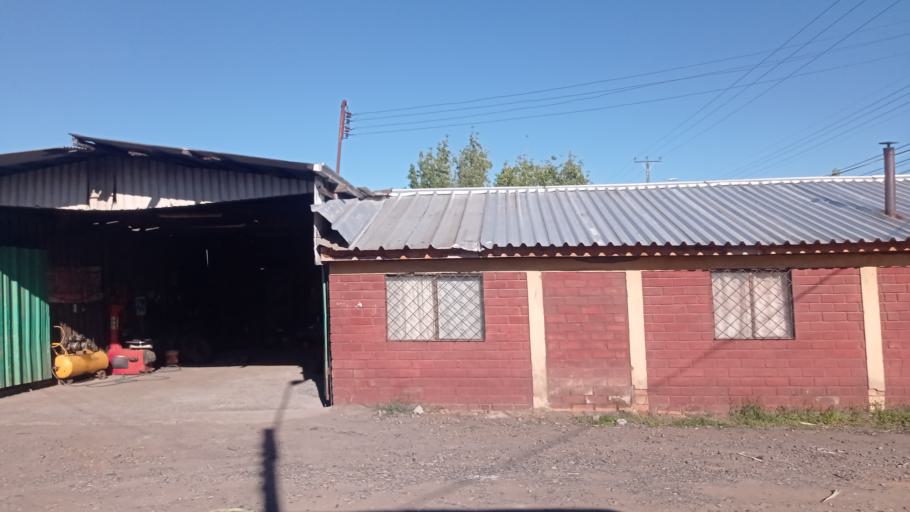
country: CL
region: Biobio
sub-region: Provincia de Biobio
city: Nacimiento
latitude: -37.5092
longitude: -72.6593
